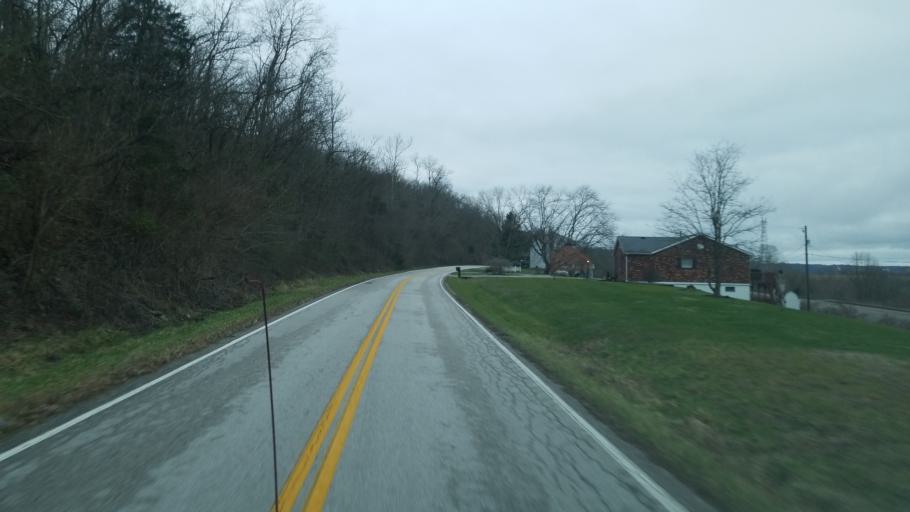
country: US
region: Kentucky
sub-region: Bracken County
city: Brooksville
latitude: 38.7878
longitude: -84.1581
